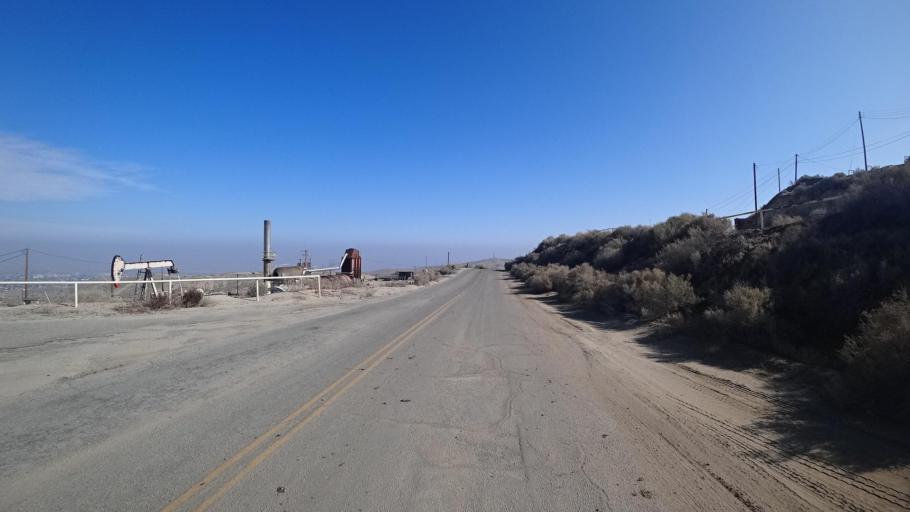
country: US
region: California
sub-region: Kern County
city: Taft Heights
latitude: 35.1209
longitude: -119.4760
